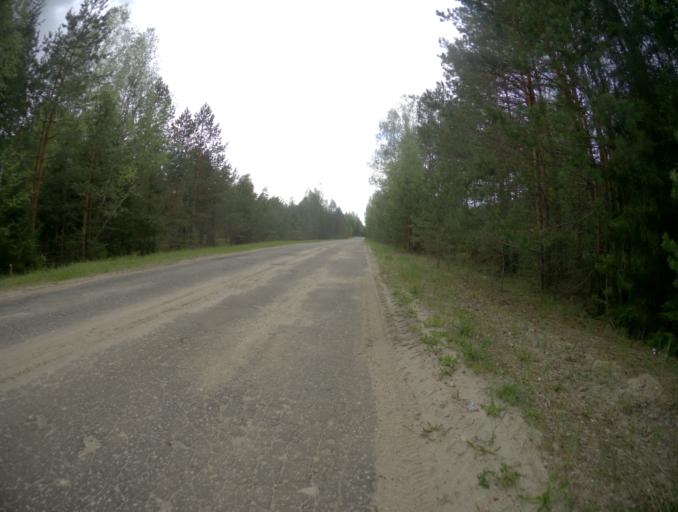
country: RU
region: Vladimir
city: Velikodvorskiy
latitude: 55.2453
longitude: 40.7066
